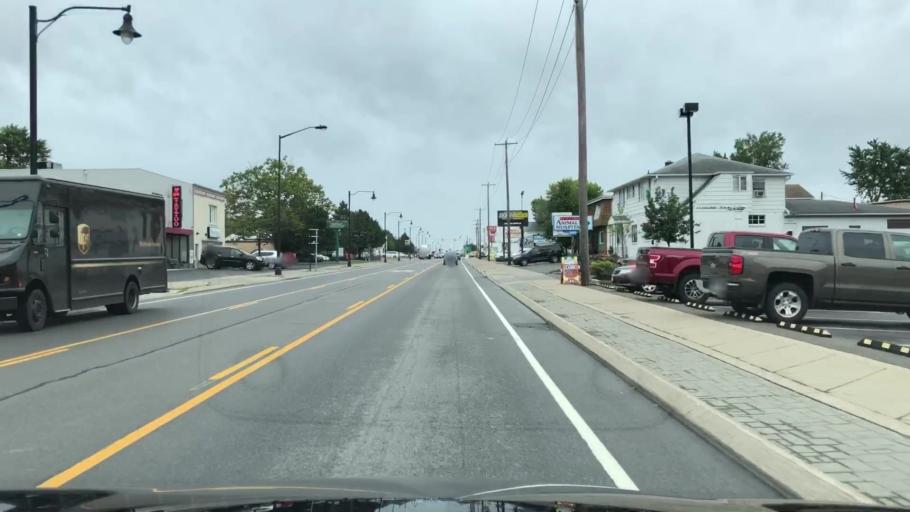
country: US
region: New York
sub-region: Erie County
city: Eggertsville
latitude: 42.9481
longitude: -78.7841
